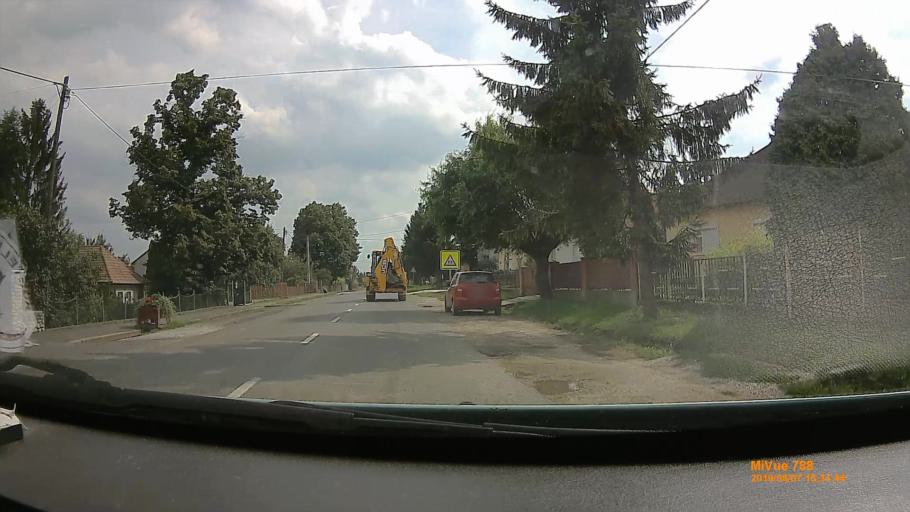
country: HU
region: Borsod-Abauj-Zemplen
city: Encs
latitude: 48.4167
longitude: 21.1739
